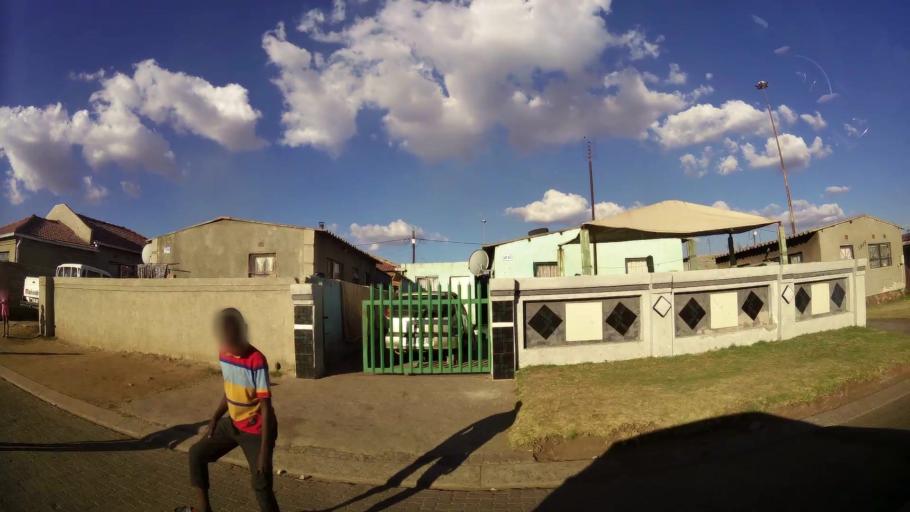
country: ZA
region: Mpumalanga
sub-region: Nkangala District Municipality
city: Witbank
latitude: -25.8738
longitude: 29.1665
